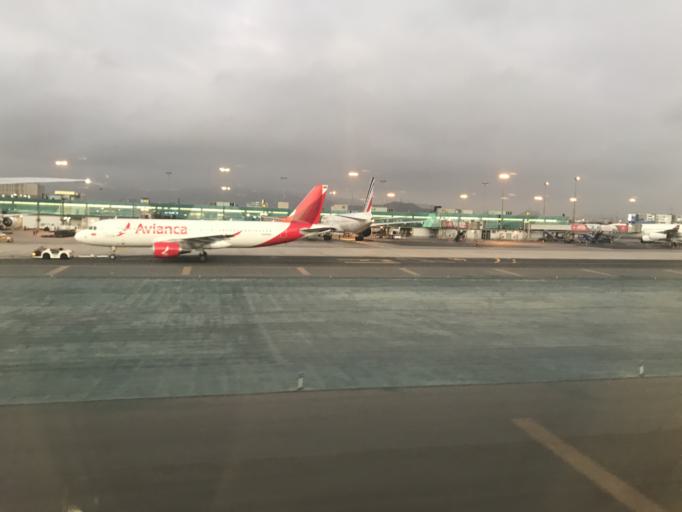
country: PE
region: Callao
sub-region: Callao
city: Callao
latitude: -12.0260
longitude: -77.1102
